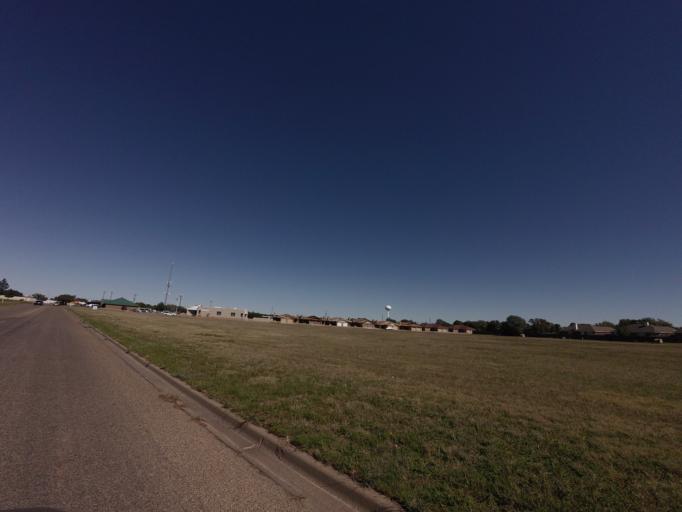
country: US
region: New Mexico
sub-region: Curry County
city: Clovis
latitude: 34.4248
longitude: -103.1911
